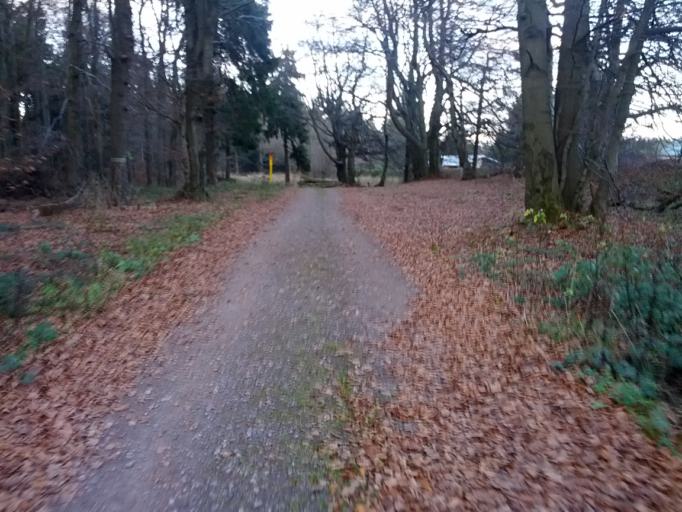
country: DE
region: Thuringia
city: Ruhla
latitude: 50.8694
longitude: 10.4074
